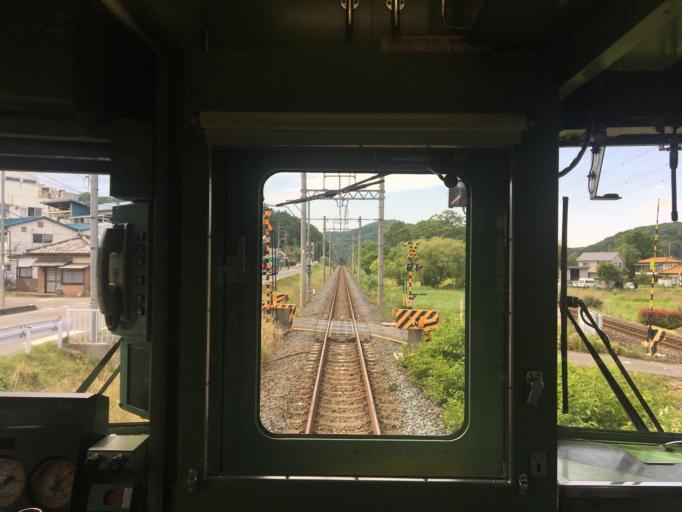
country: JP
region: Saitama
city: Ogawa
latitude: 36.0676
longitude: 139.2436
